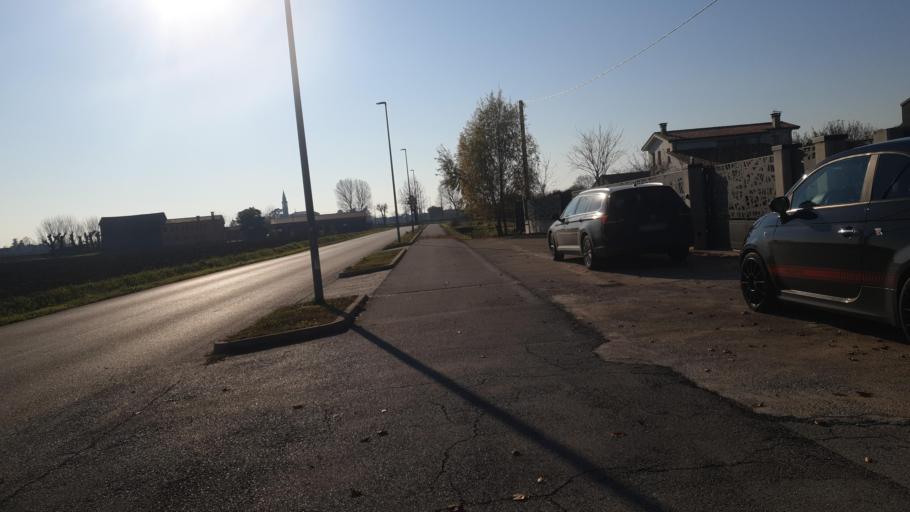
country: IT
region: Veneto
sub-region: Provincia di Padova
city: Due Carrare
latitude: 45.3006
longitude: 11.8264
